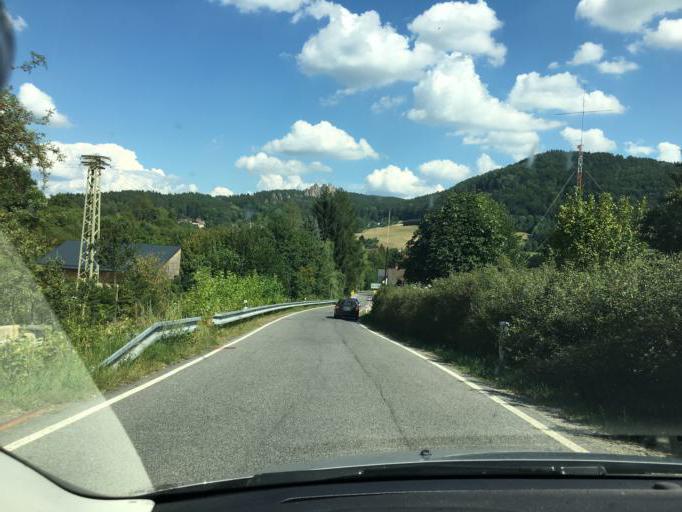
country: CZ
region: Liberecky
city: Mala Skala
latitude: 50.6396
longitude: 15.1848
